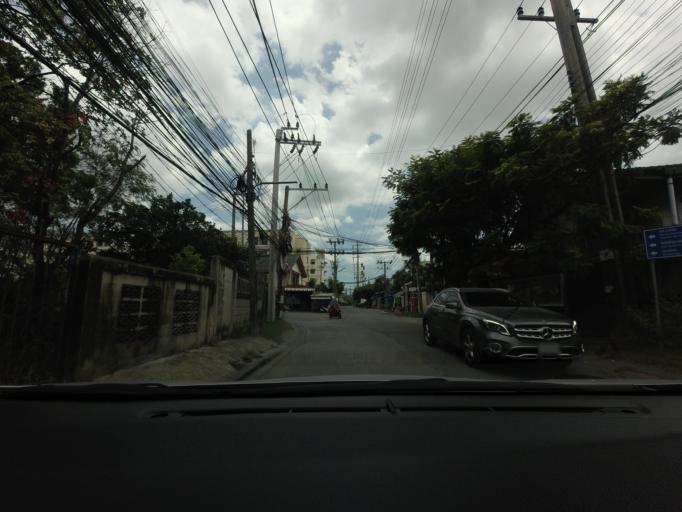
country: TH
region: Samut Prakan
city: Phra Samut Chedi
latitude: 13.6257
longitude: 100.5620
